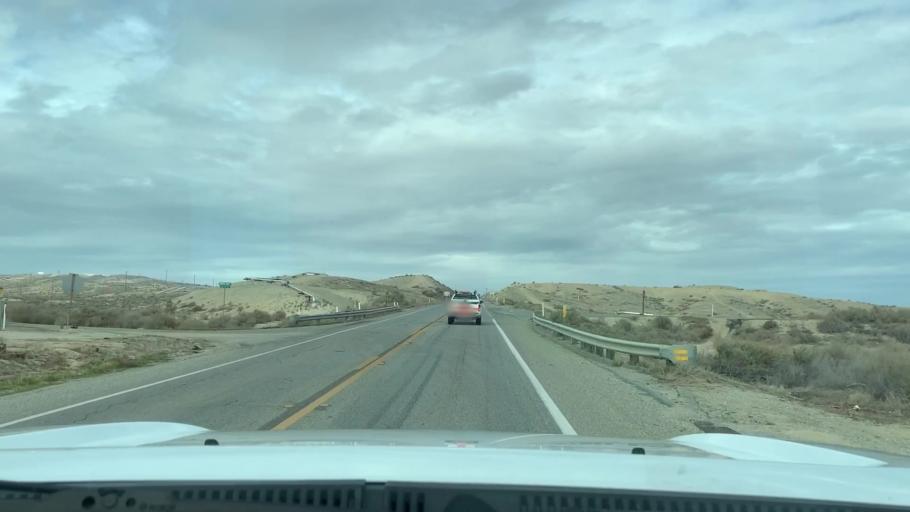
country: US
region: California
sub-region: Kern County
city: Maricopa
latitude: 35.0957
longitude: -119.4106
